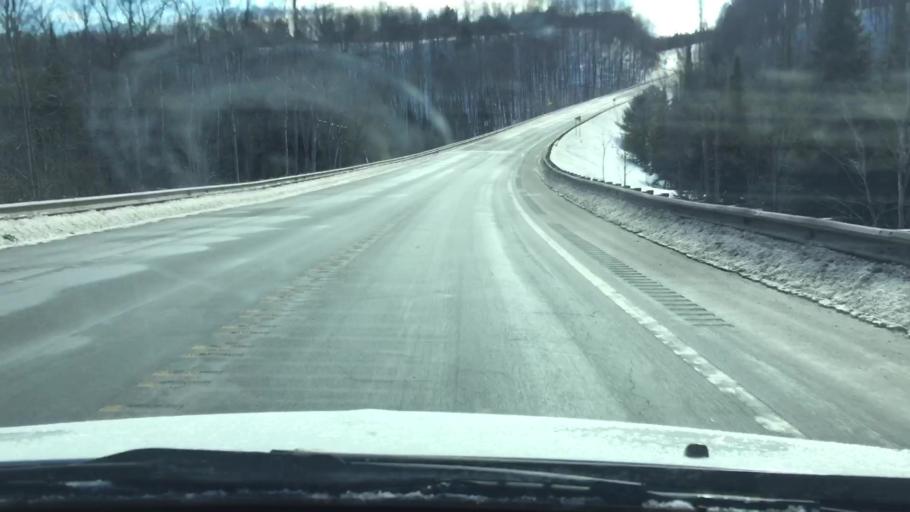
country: US
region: Michigan
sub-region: Antrim County
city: Mancelona
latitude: 44.9576
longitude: -85.0504
